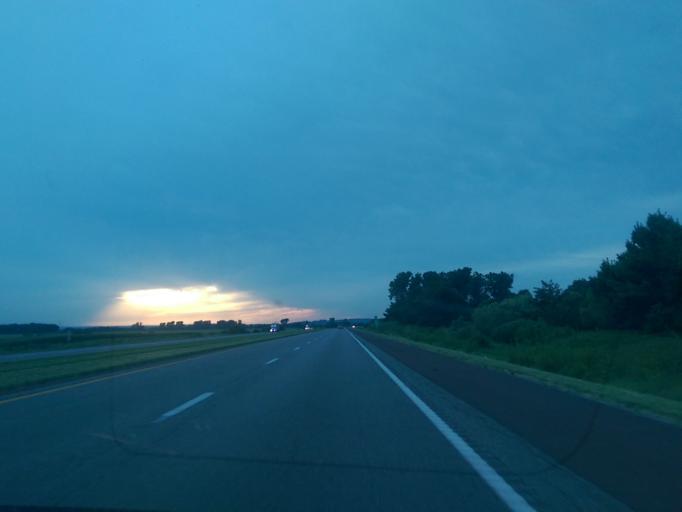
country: US
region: Missouri
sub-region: Holt County
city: Mound City
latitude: 40.1674
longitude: -95.2921
